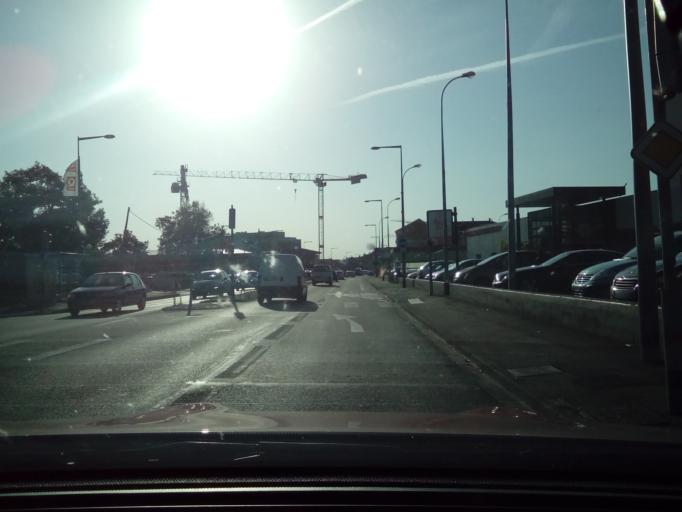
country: FR
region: Rhone-Alpes
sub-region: Departement du Rhone
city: Bron
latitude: 45.7507
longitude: 4.9093
